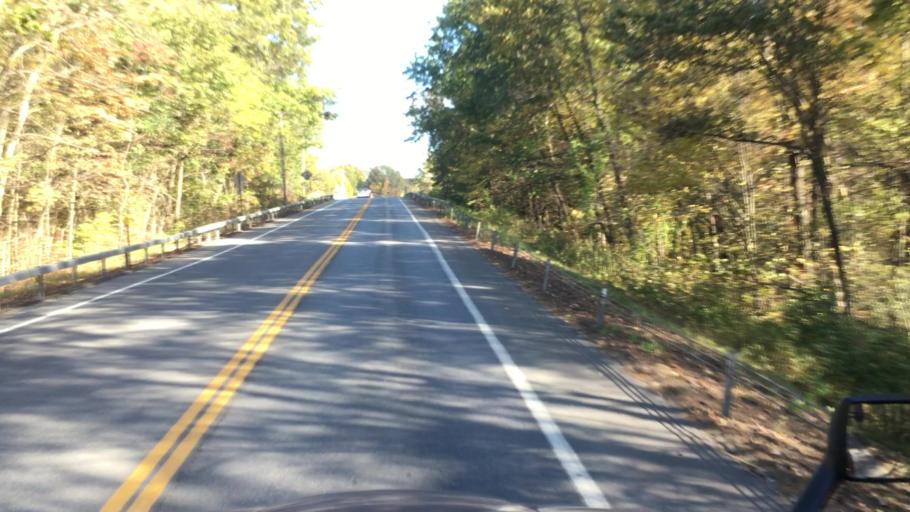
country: US
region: New York
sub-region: Saratoga County
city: Milton
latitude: 43.0598
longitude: -73.8203
